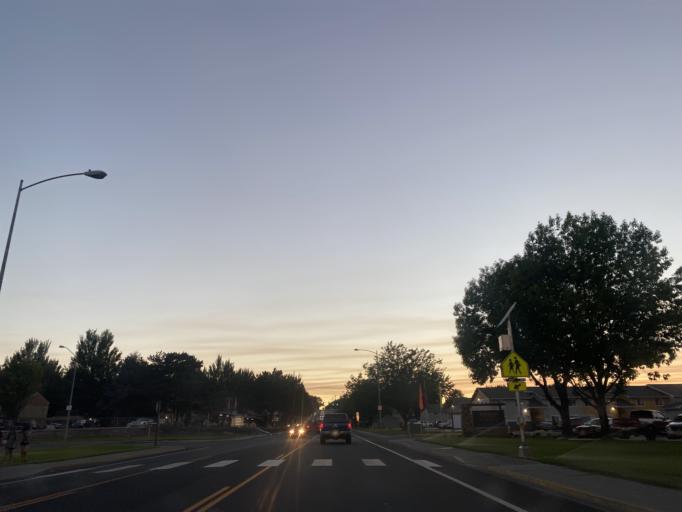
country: US
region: Washington
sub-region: Benton County
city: Kennewick
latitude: 46.1985
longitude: -119.1325
